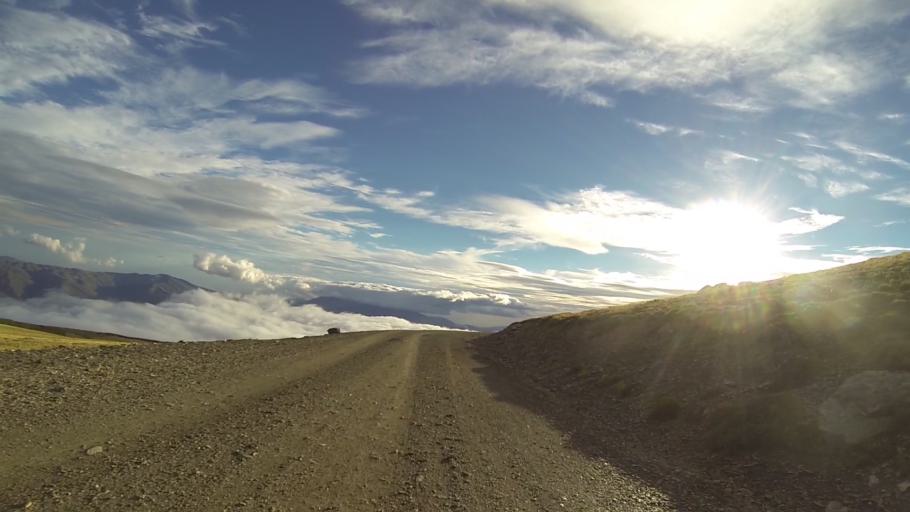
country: ES
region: Andalusia
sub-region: Provincia de Granada
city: Portugos
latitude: 36.9850
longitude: -3.3152
